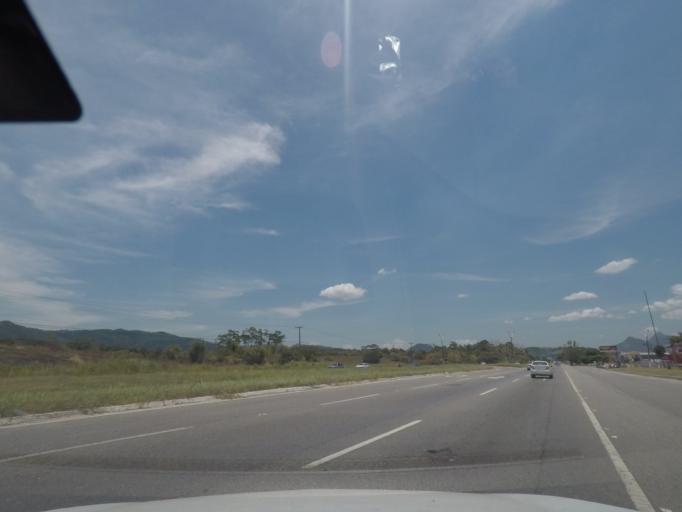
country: BR
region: Rio de Janeiro
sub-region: Marica
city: Marica
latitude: -22.9145
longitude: -42.8469
